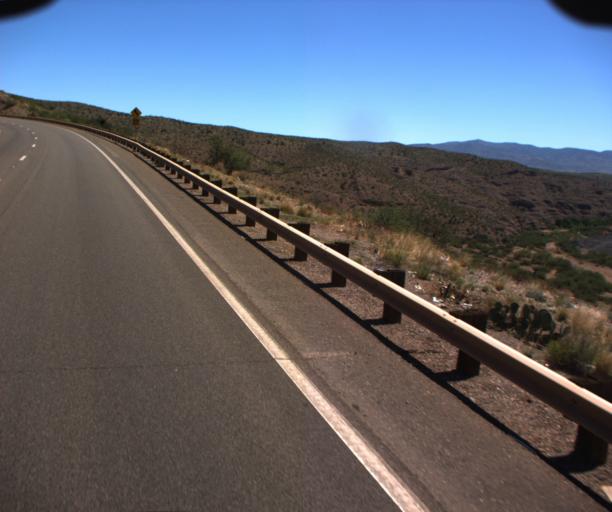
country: US
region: Arizona
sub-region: Greenlee County
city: Clifton
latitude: 33.0282
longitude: -109.2980
